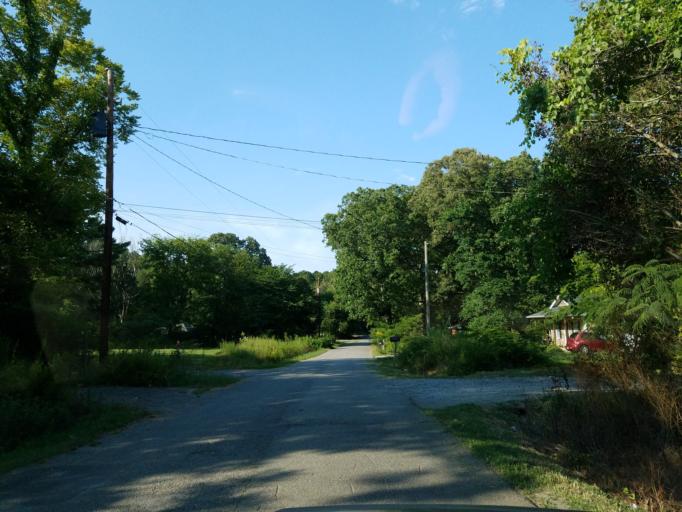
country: US
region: Georgia
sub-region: Bartow County
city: Cartersville
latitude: 34.2117
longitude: -84.7945
